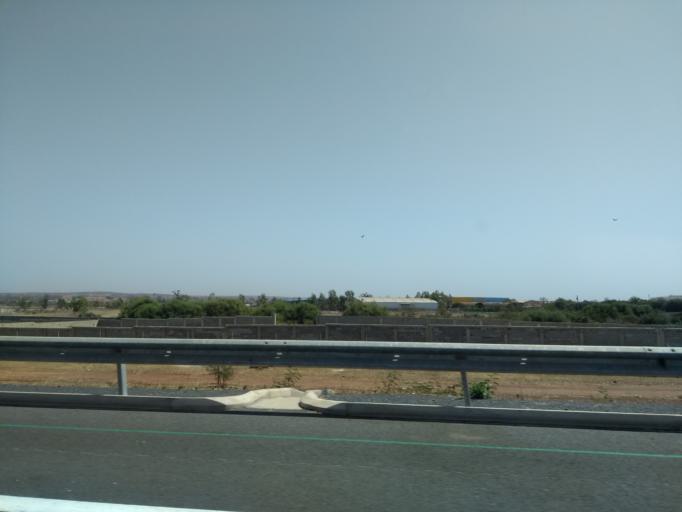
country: SN
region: Thies
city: Pout
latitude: 14.7351
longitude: -17.1699
